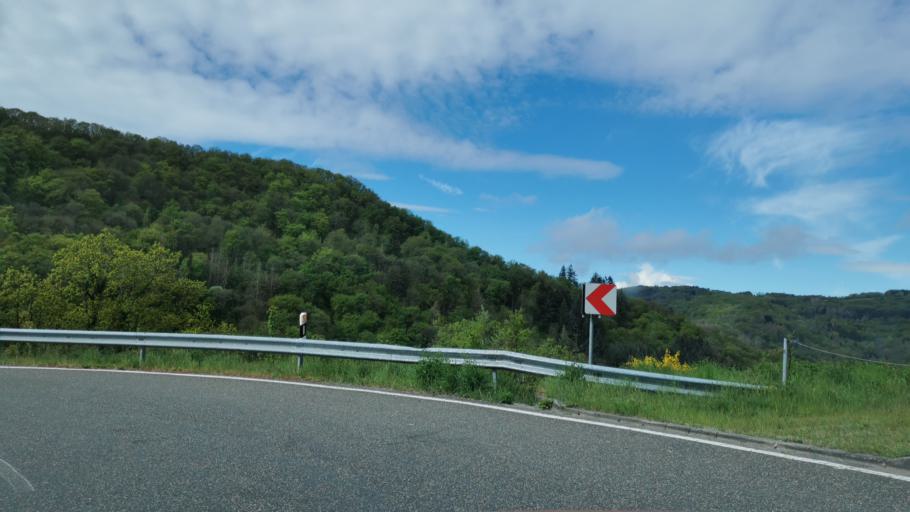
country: DE
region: Rheinland-Pfalz
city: Traben-Trarbach
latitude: 49.9412
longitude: 7.1219
